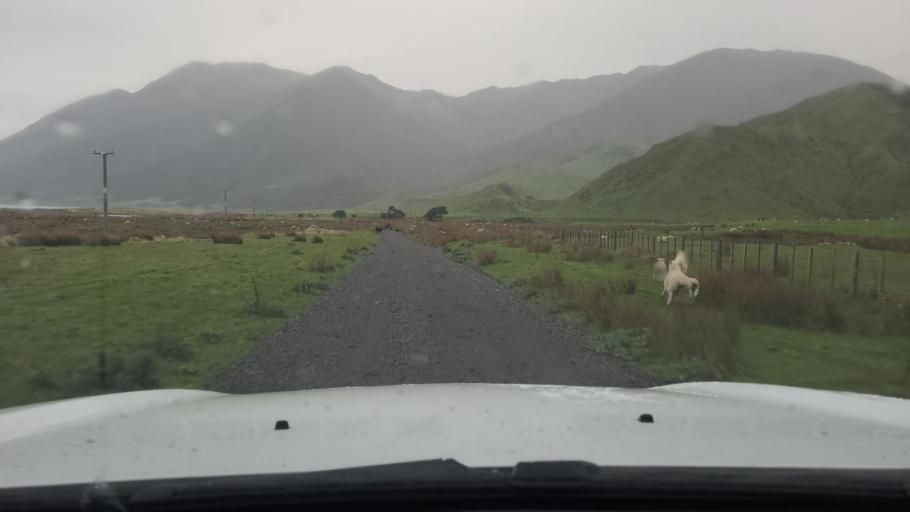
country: NZ
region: Wellington
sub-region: South Wairarapa District
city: Waipawa
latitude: -41.5665
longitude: 175.3863
